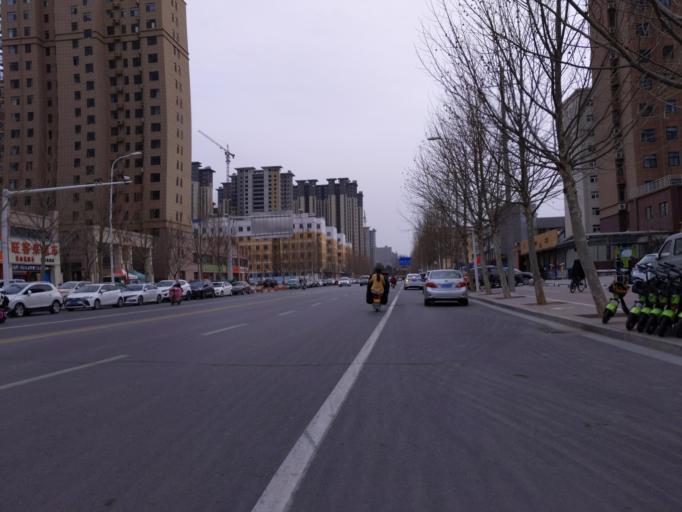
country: CN
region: Henan Sheng
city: Zhongyuanlu
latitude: 35.7608
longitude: 115.0743
